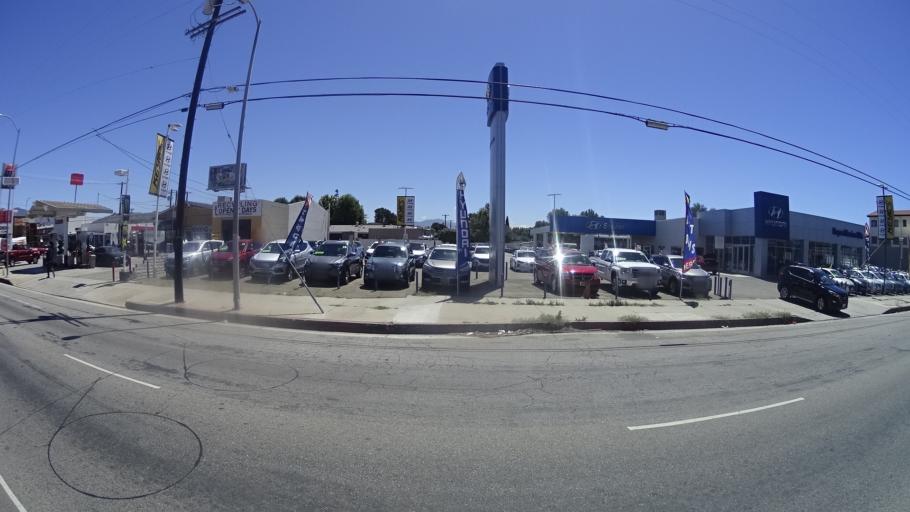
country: US
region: California
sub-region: Los Angeles County
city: San Fernando
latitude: 34.2567
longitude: -118.4673
